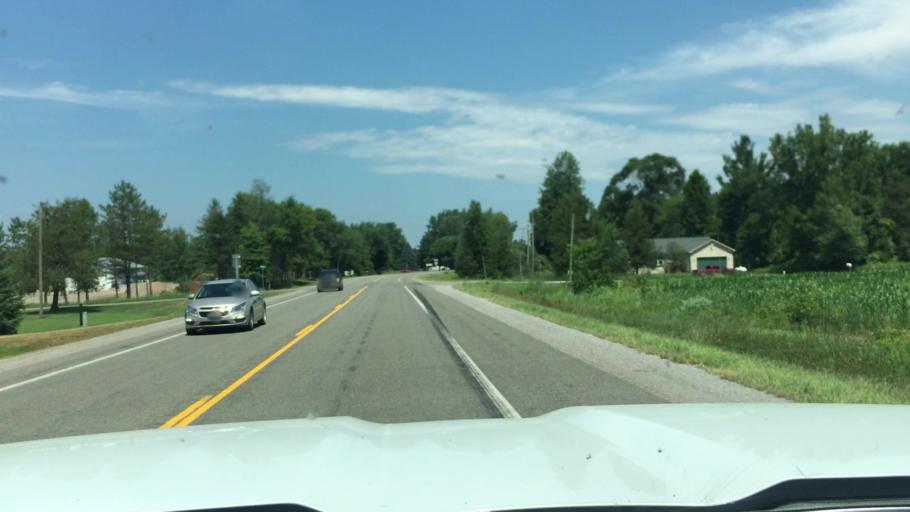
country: US
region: Michigan
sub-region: Saginaw County
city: Chesaning
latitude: 43.2146
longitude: -84.1694
